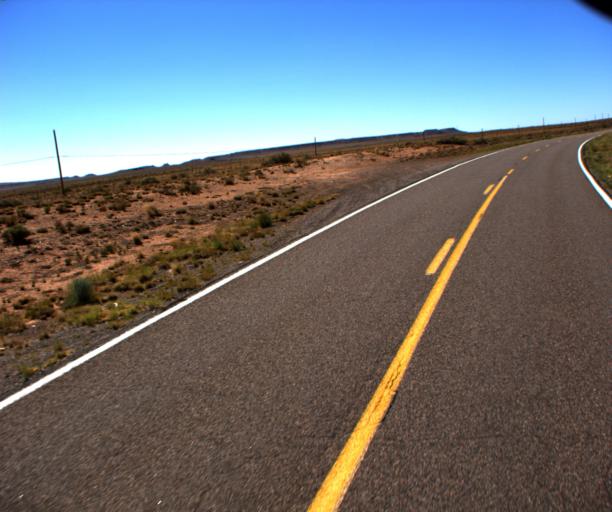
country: US
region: Arizona
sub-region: Coconino County
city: LeChee
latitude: 35.1074
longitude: -110.8651
